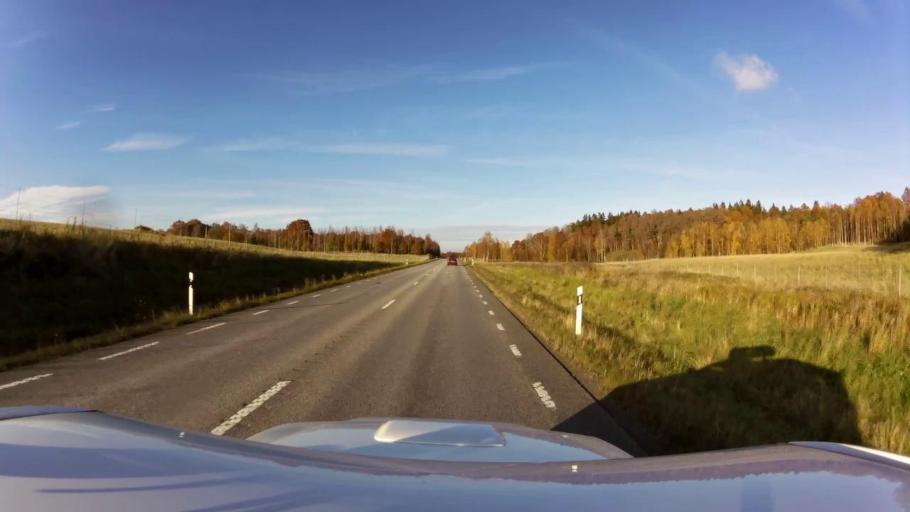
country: SE
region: OEstergoetland
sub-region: Kinda Kommun
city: Rimforsa
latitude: 58.2019
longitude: 15.6682
